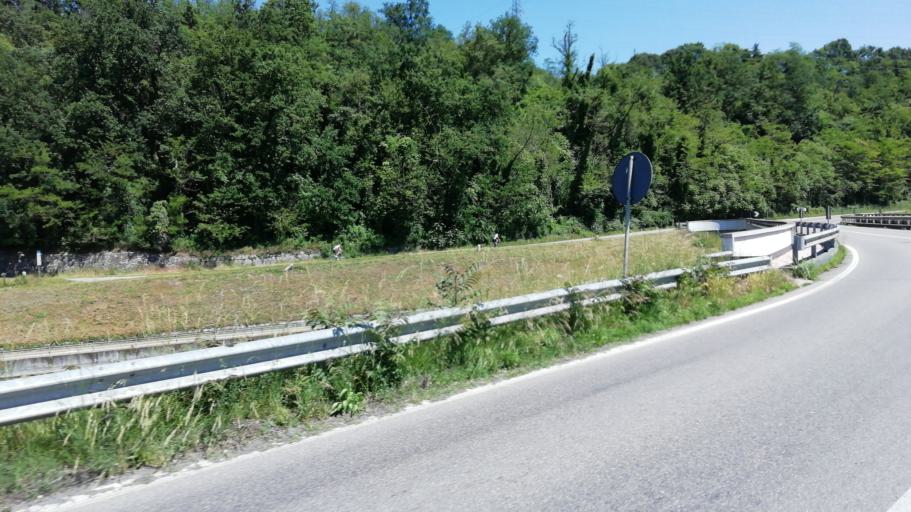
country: IT
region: Lombardy
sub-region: Provincia di Varese
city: Vizzola Ticino
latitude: 45.5869
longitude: 8.7061
